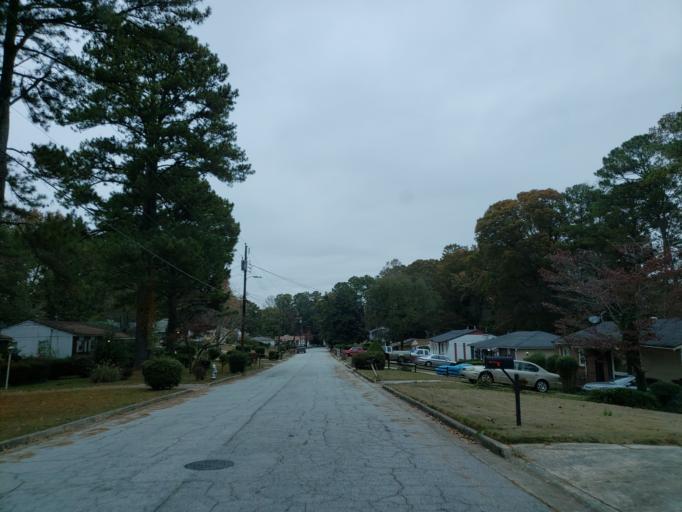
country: US
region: Georgia
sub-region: Cobb County
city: Mableton
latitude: 33.7761
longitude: -84.5118
